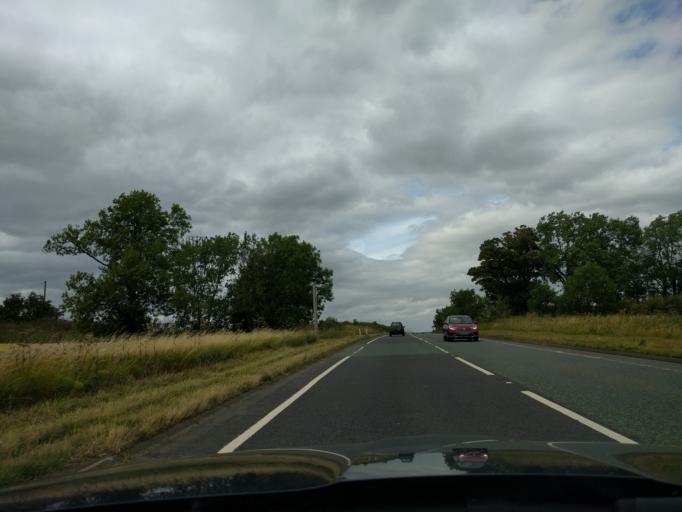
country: GB
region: England
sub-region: Northumberland
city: Ellingham
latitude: 55.5336
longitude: -1.7738
